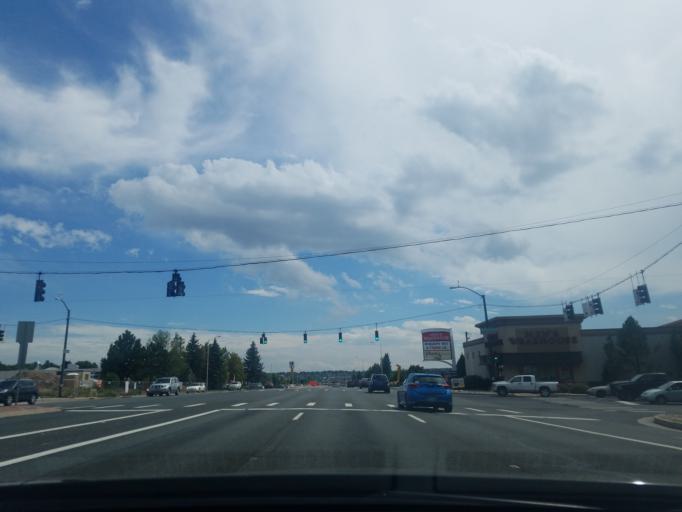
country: US
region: Colorado
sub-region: El Paso County
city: Air Force Academy
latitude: 38.9413
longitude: -104.7995
